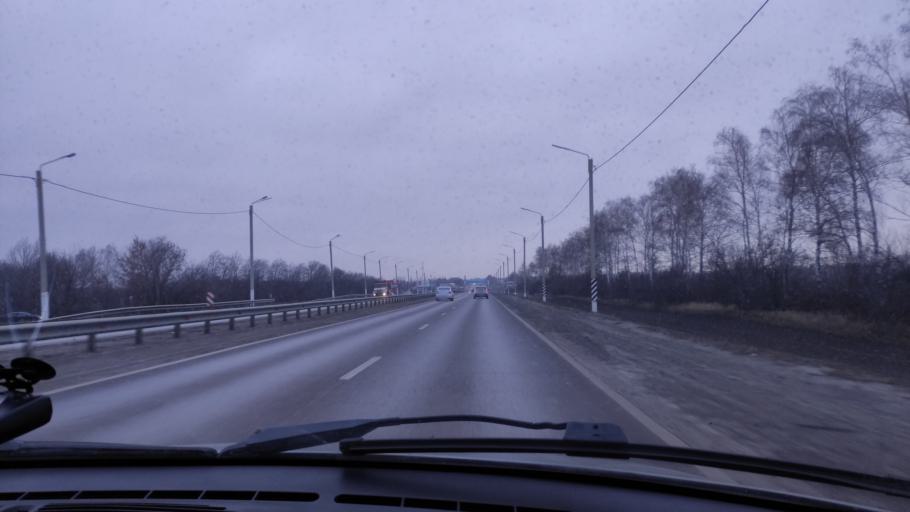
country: RU
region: Tambov
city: Komsomolets
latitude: 52.7268
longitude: 41.3388
